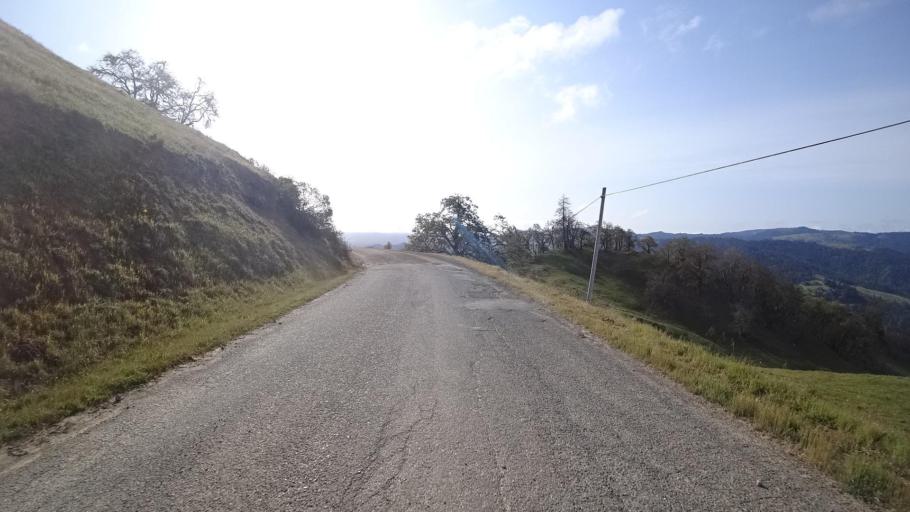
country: US
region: California
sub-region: Humboldt County
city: Hydesville
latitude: 40.6389
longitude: -123.9015
